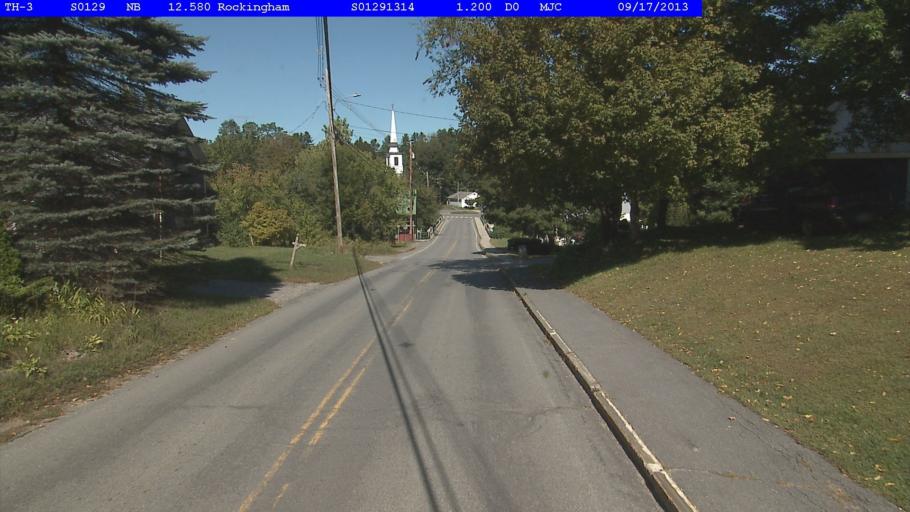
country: US
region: Vermont
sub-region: Windham County
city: Rockingham
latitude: 43.1368
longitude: -72.5103
